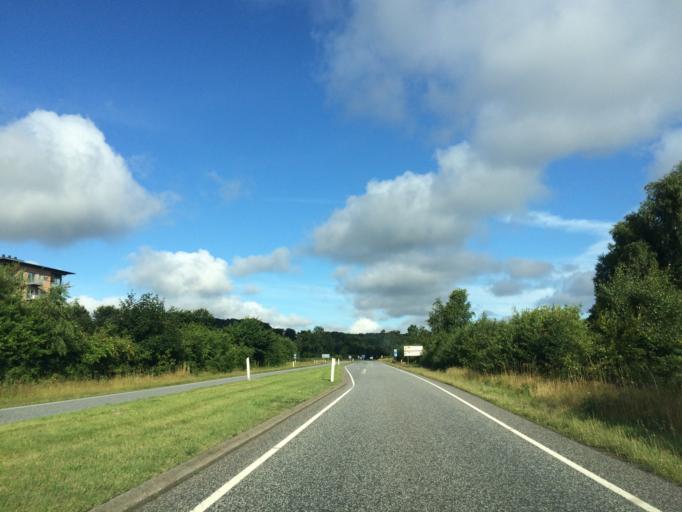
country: DK
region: Central Jutland
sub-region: Viborg Kommune
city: Bjerringbro
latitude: 56.3124
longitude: 9.5884
